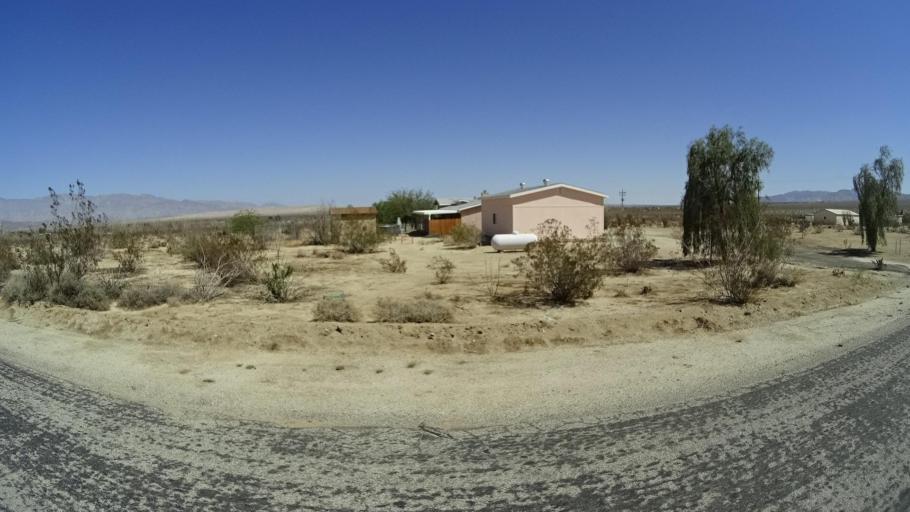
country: US
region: California
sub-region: San Diego County
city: Borrego Springs
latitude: 33.2215
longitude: -116.3652
